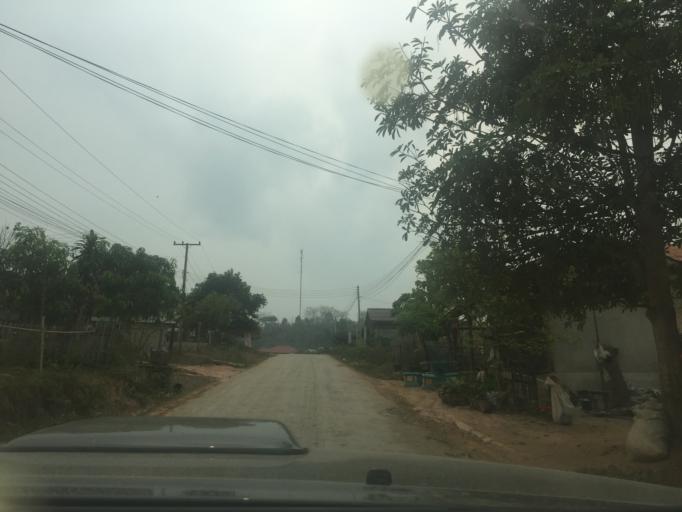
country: LA
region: Vientiane
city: Muang Sanakham
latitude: 18.4026
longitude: 101.5108
